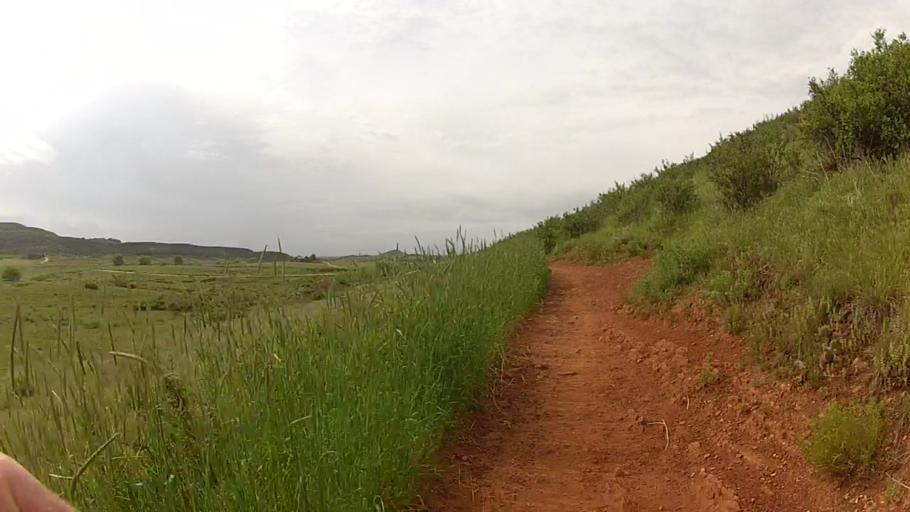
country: US
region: Colorado
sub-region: Larimer County
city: Loveland
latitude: 40.4162
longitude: -105.1546
